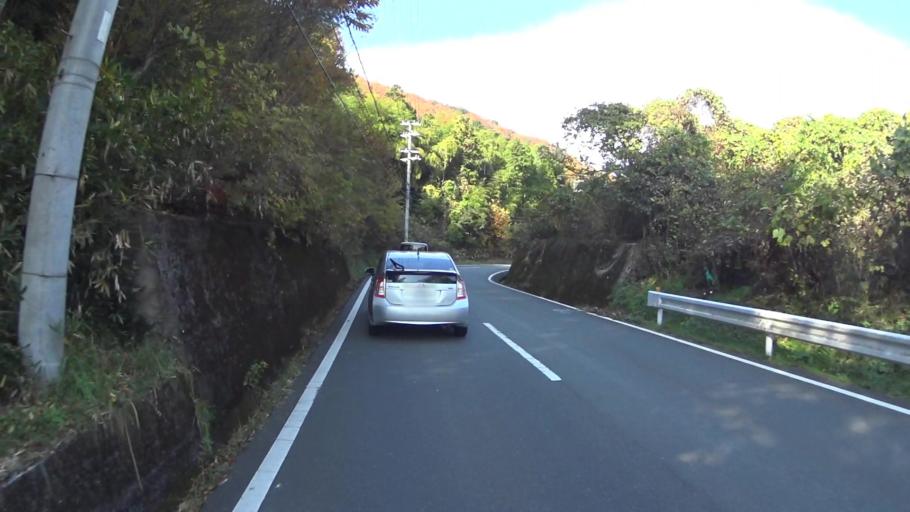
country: JP
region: Kyoto
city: Maizuru
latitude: 35.5277
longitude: 135.3921
